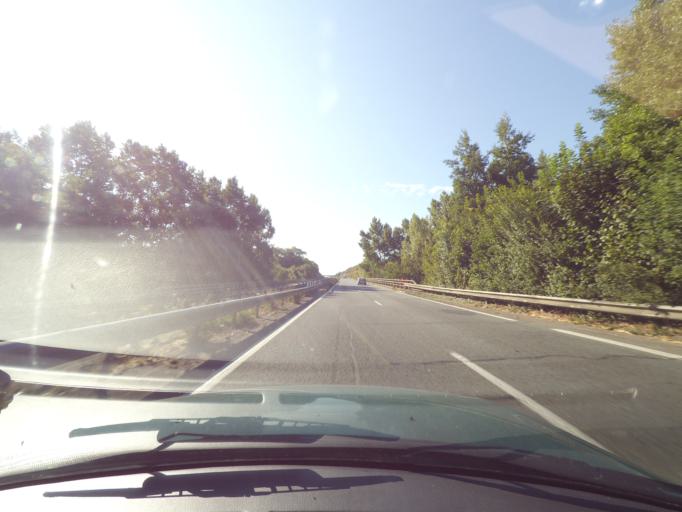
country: FR
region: Poitou-Charentes
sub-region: Departement de la Vienne
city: Migne-Auxances
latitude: 46.6263
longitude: 0.2980
